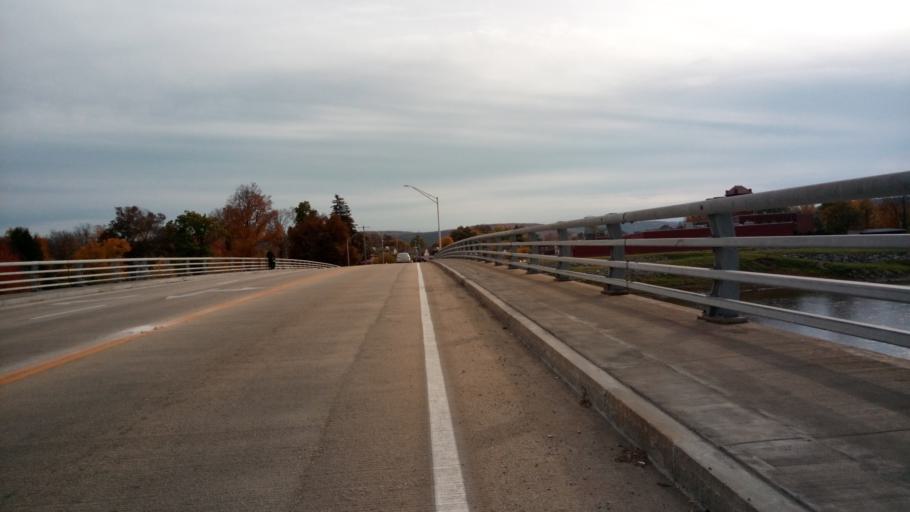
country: US
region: New York
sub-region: Chemung County
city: Elmira
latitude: 42.0880
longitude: -76.7980
